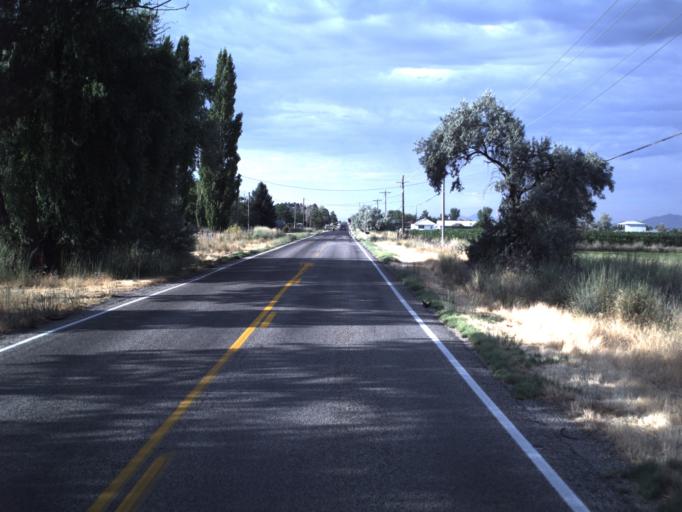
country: US
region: Utah
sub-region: Weber County
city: West Haven
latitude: 41.2192
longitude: -112.0929
